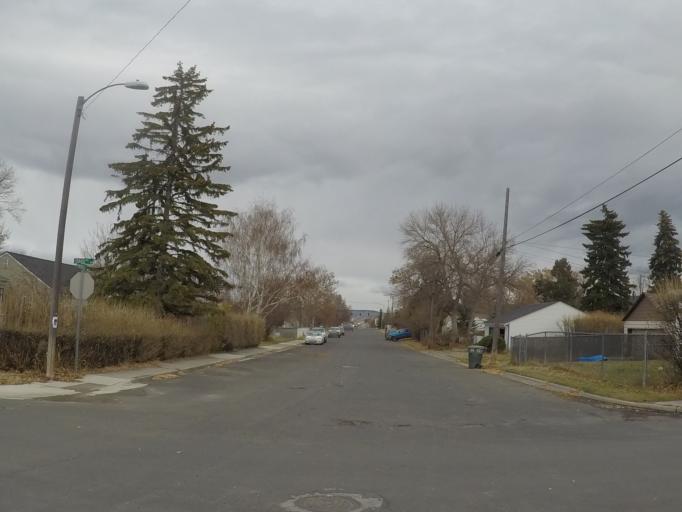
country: US
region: Montana
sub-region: Lewis and Clark County
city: Helena
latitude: 46.5910
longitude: -112.0240
